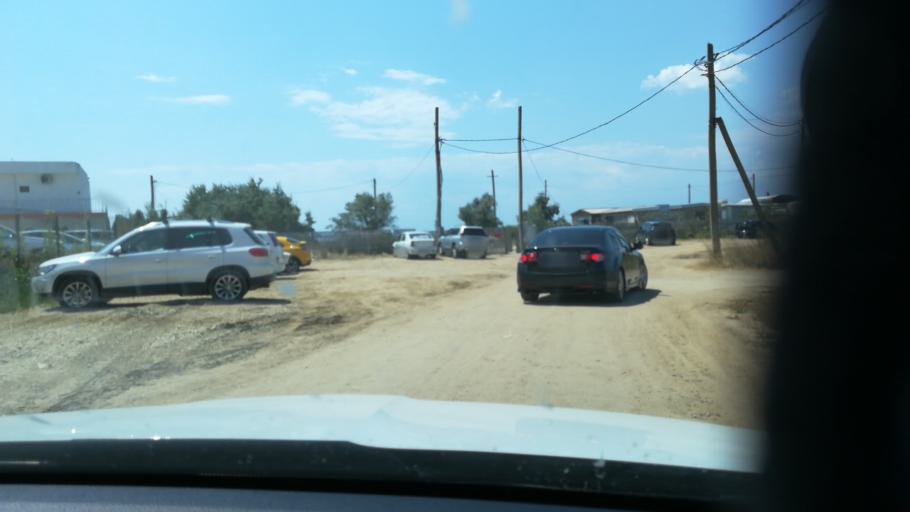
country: RU
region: Krasnodarskiy
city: Vyshestebliyevskaya
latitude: 45.1123
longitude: 36.8728
